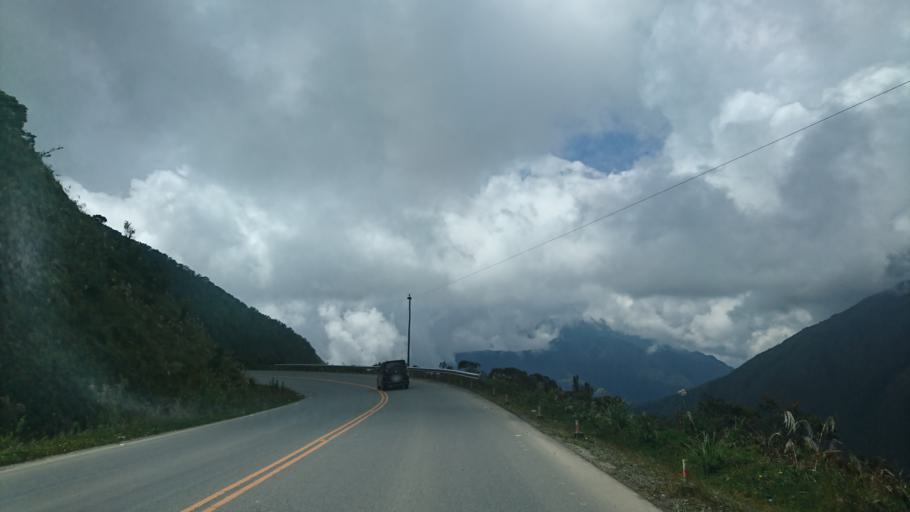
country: BO
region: La Paz
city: Coroico
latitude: -16.2920
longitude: -67.8641
